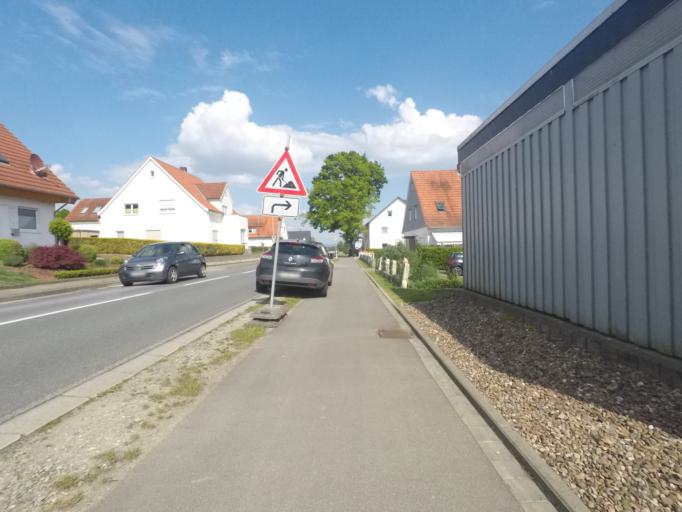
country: DE
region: North Rhine-Westphalia
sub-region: Regierungsbezirk Detmold
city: Kirchlengern
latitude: 52.2181
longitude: 8.6482
